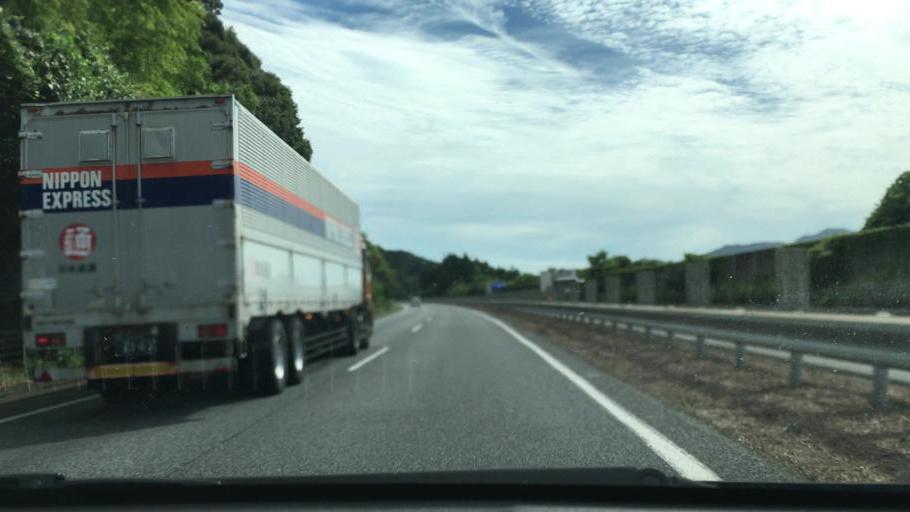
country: JP
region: Yamaguchi
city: Ogori-shimogo
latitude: 34.1293
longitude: 131.4229
